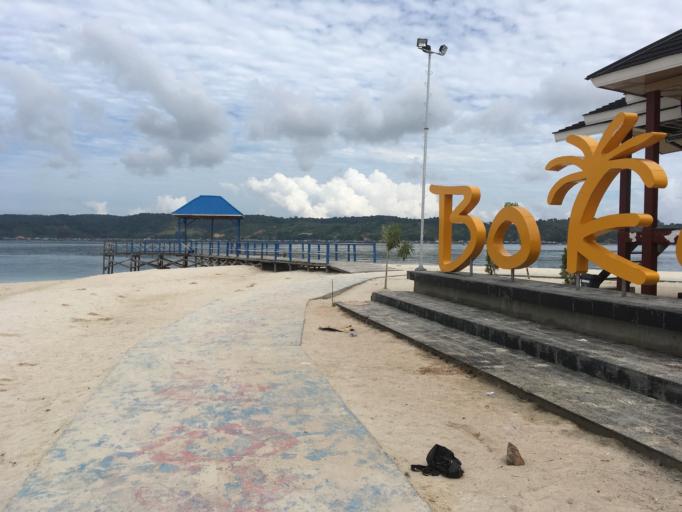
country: ID
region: Sulawesi Tenggara
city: Kendari
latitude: -3.9399
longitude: 122.6591
